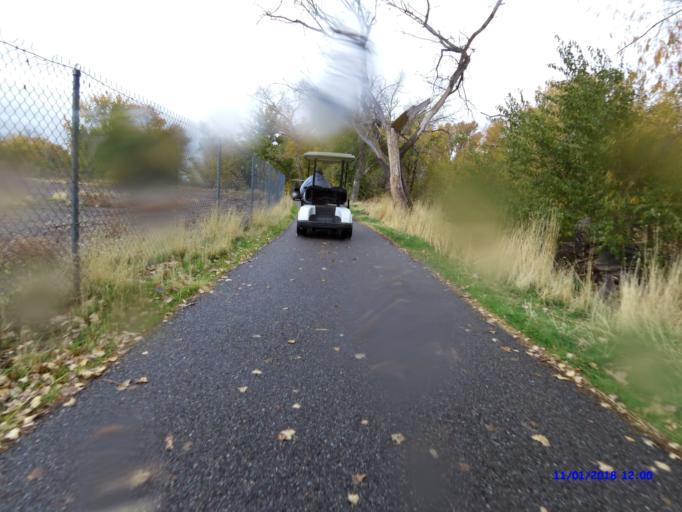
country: US
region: Utah
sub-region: Weber County
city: Ogden
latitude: 41.2318
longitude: -112.0017
